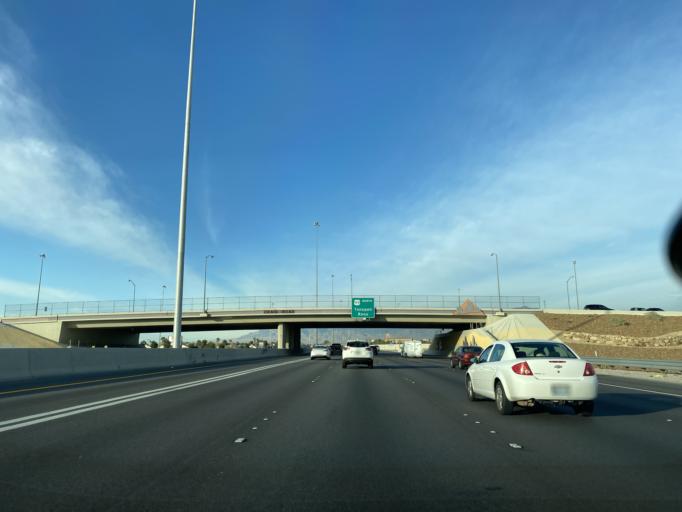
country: US
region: Nevada
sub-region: Clark County
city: Las Vegas
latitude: 36.2394
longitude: -115.2467
